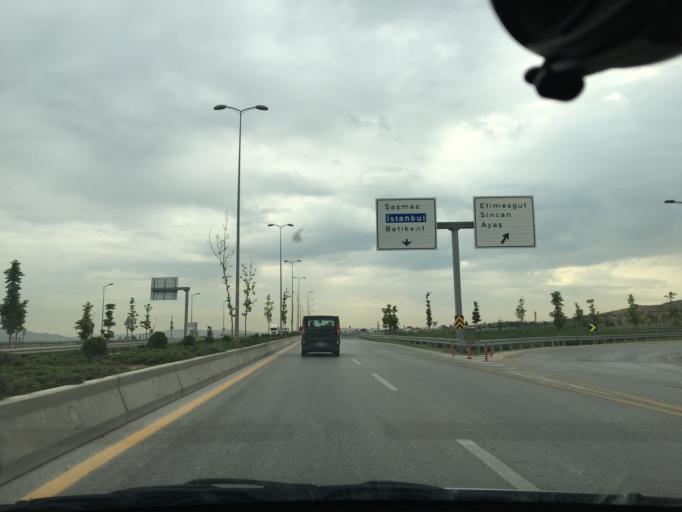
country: TR
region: Ankara
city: Batikent
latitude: 39.9259
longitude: 32.7083
